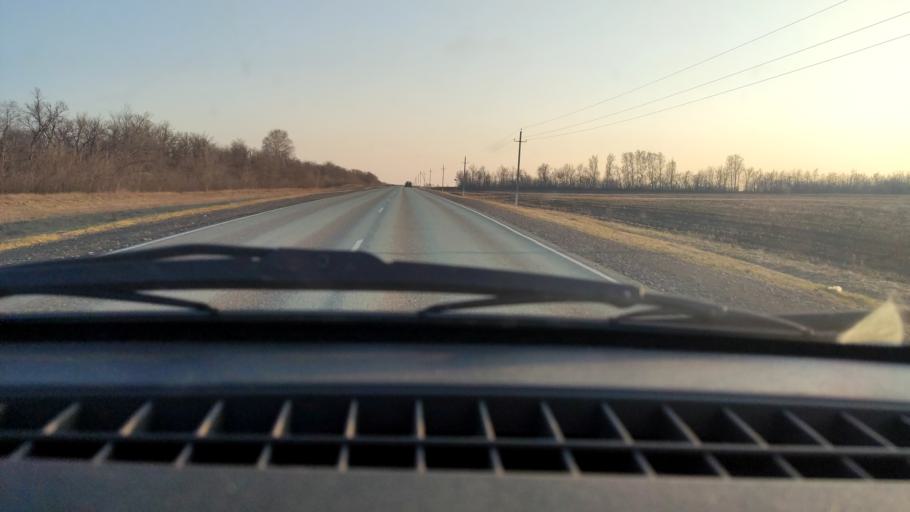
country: RU
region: Bashkortostan
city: Davlekanovo
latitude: 54.3201
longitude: 55.1554
